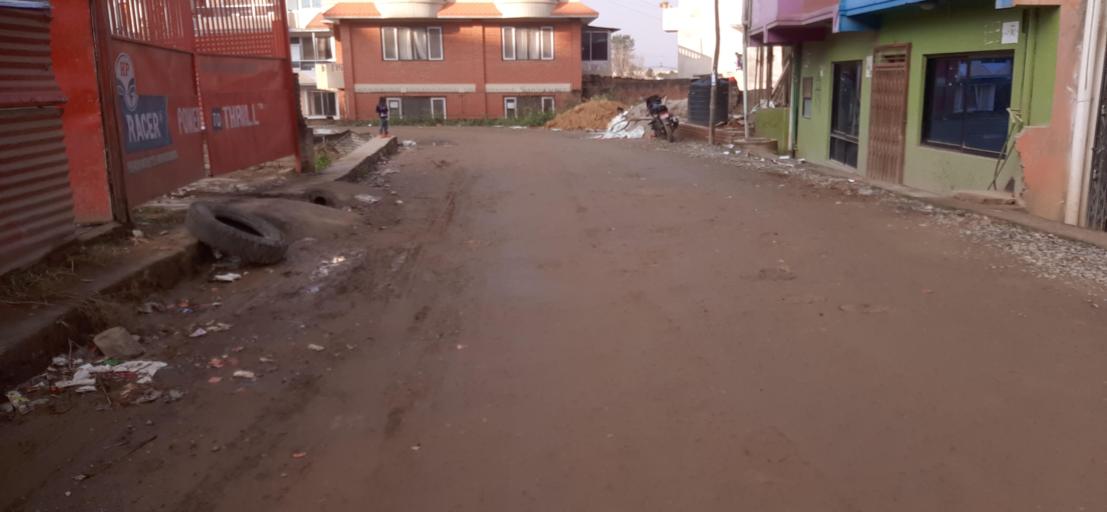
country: NP
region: Central Region
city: Kirtipur
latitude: 27.6742
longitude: 85.2821
